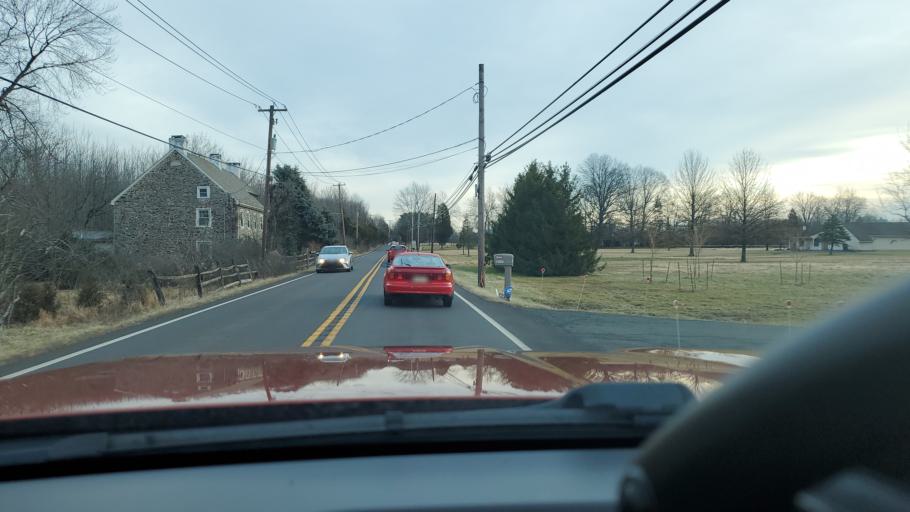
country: US
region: Pennsylvania
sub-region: Montgomery County
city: Telford
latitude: 40.3542
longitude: -75.3638
